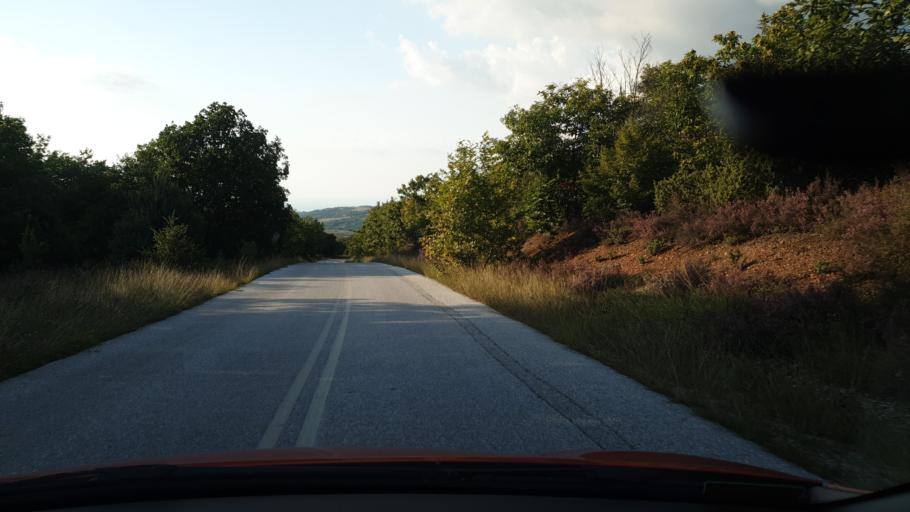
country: GR
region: Central Macedonia
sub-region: Nomos Chalkidikis
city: Galatista
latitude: 40.5155
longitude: 23.2704
